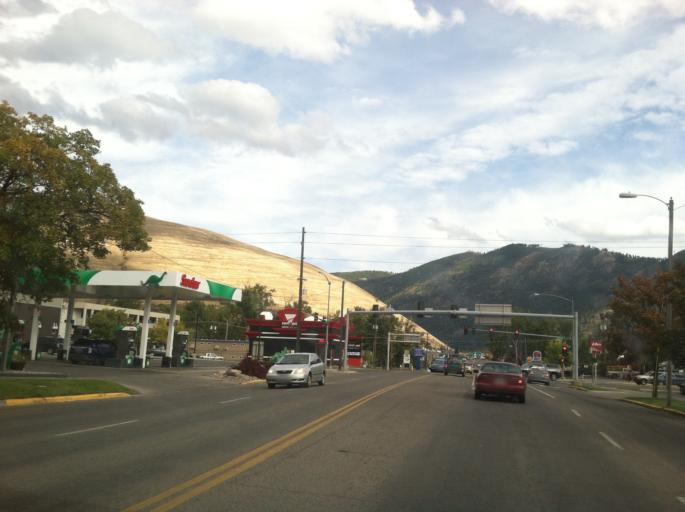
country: US
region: Montana
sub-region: Missoula County
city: Missoula
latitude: 46.8703
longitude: -113.9881
